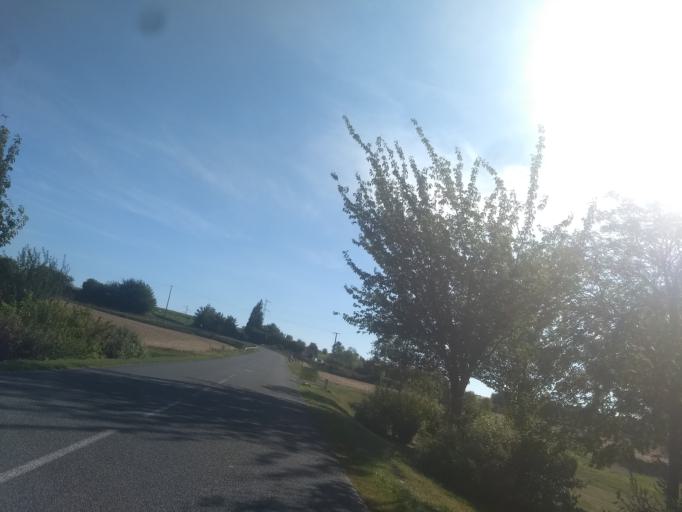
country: FR
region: Nord-Pas-de-Calais
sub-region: Departement du Pas-de-Calais
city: Roeux
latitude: 50.2892
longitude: 2.8994
